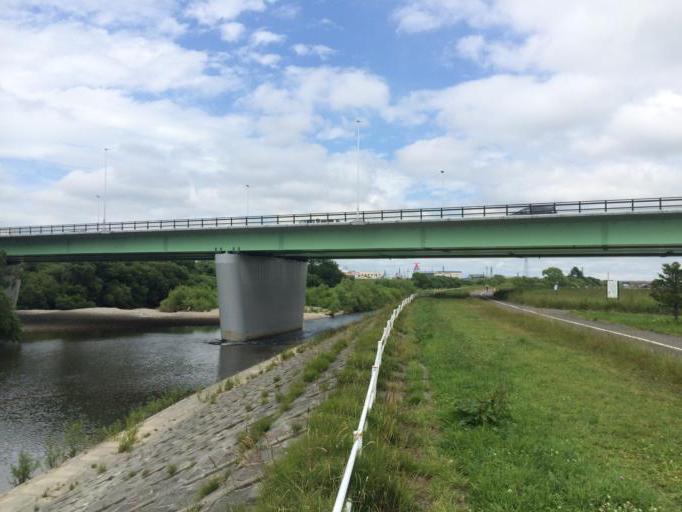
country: JP
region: Hokkaido
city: Sapporo
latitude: 43.0739
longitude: 141.4037
